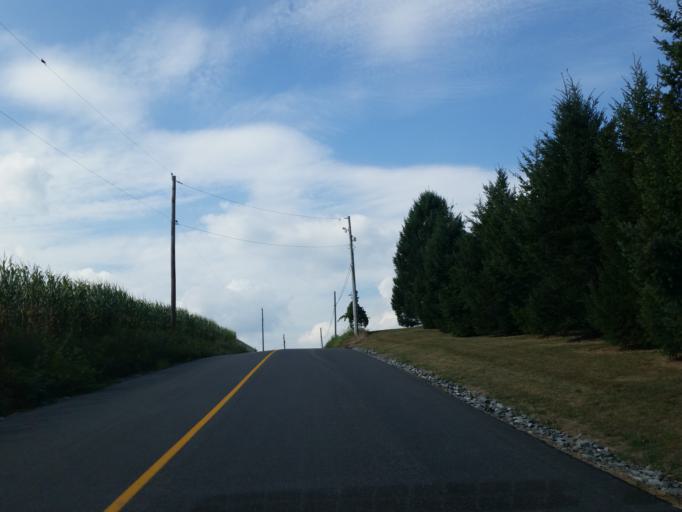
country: US
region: Pennsylvania
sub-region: Lancaster County
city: Mount Joy
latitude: 40.1452
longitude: -76.4643
